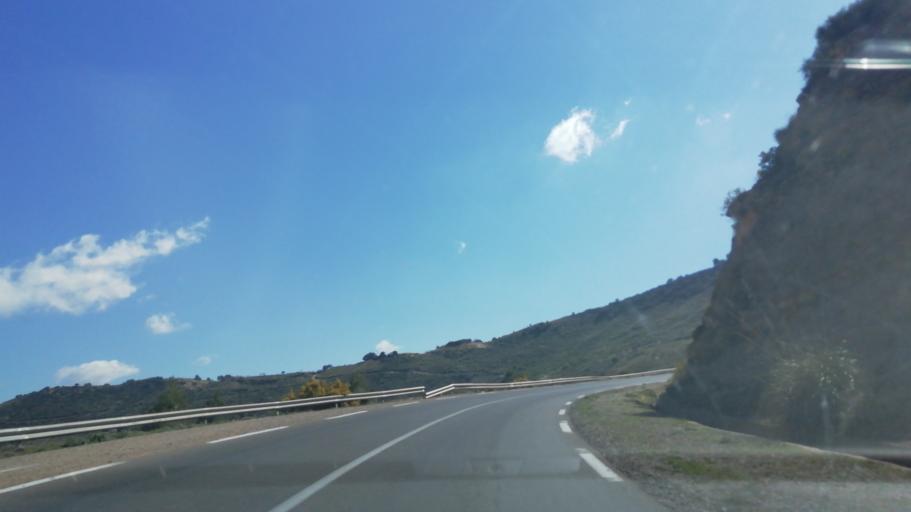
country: DZ
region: Mascara
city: Mascara
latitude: 35.4815
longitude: 0.1595
